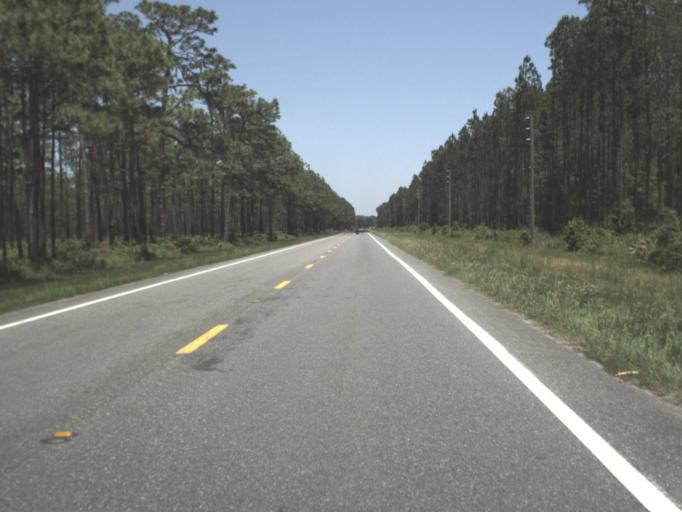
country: US
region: Florida
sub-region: Columbia County
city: Watertown
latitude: 30.1972
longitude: -82.4925
